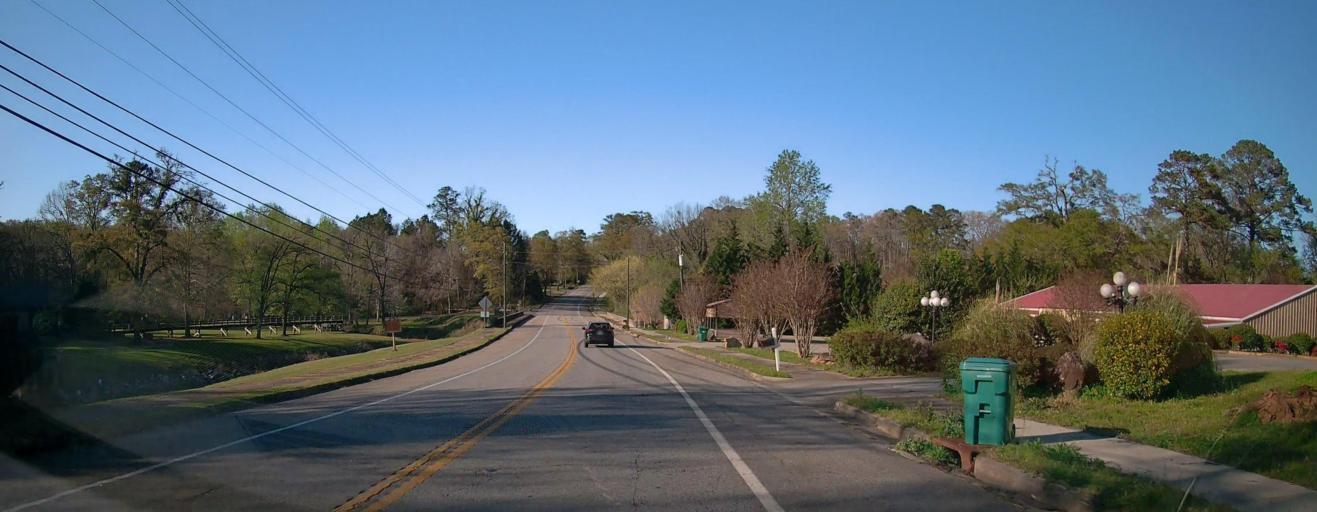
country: US
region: Georgia
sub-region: Butts County
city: Indian Springs
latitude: 33.2460
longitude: -83.9204
